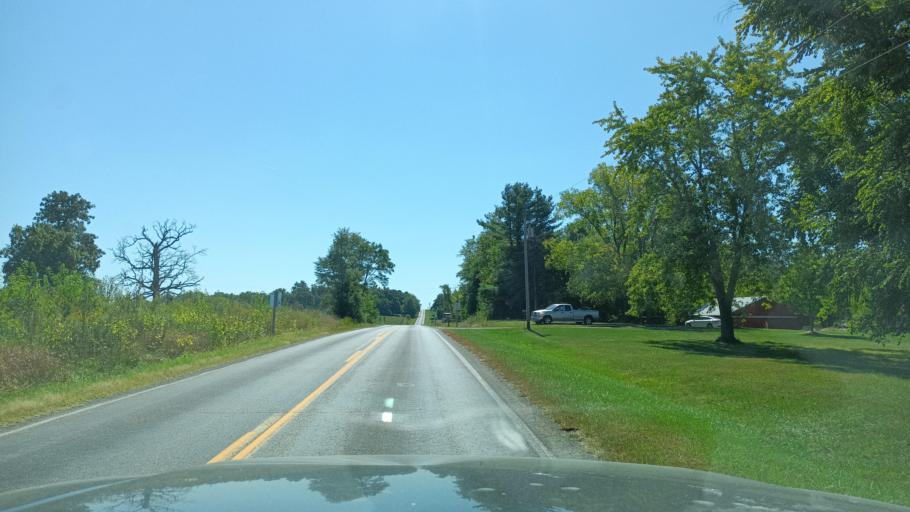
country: US
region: Illinois
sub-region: McLean County
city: Danvers
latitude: 40.5973
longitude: -89.2028
